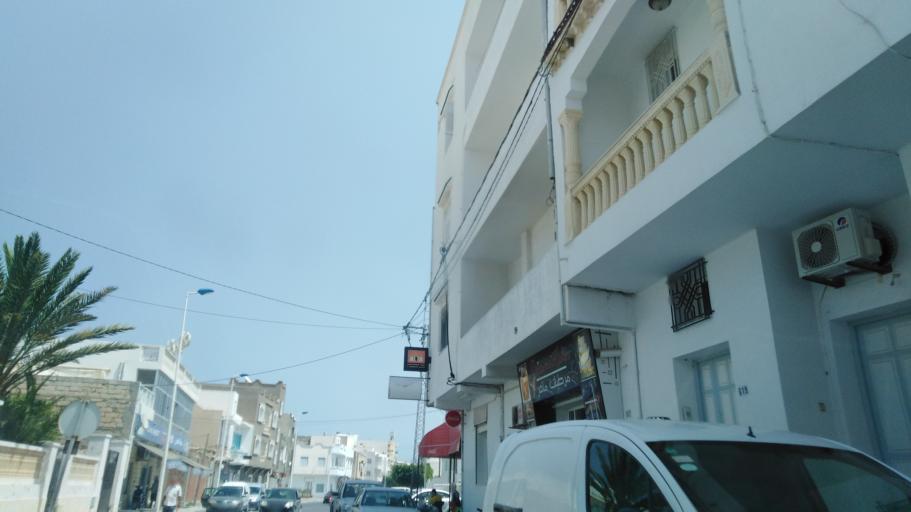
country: TN
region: Al Mahdiyah
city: Mahdia
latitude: 35.5135
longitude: 11.0443
